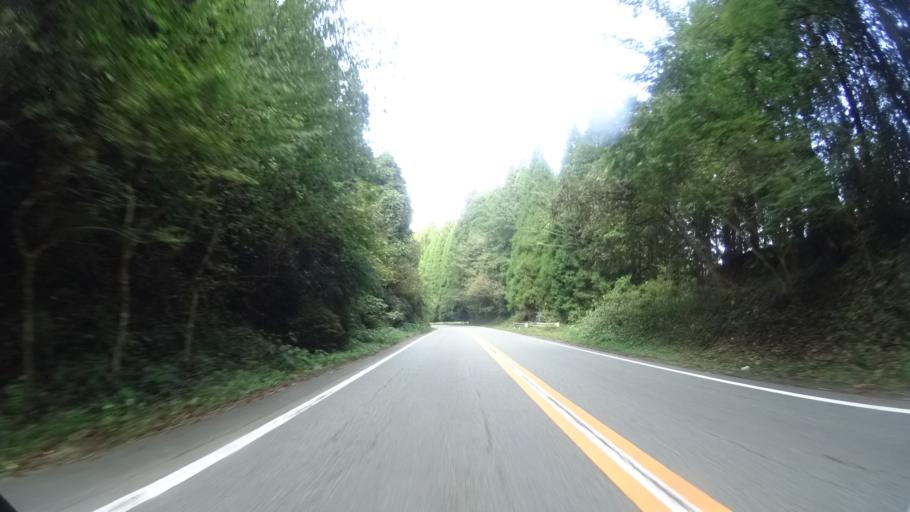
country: JP
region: Kumamoto
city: Aso
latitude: 33.0726
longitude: 131.0636
